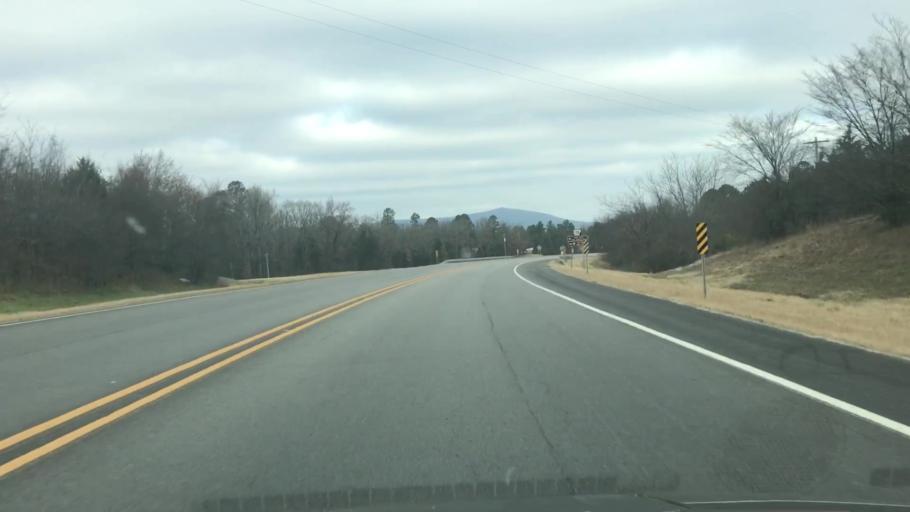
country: US
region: Arkansas
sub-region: Scott County
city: Waldron
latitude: 34.8848
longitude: -94.1066
